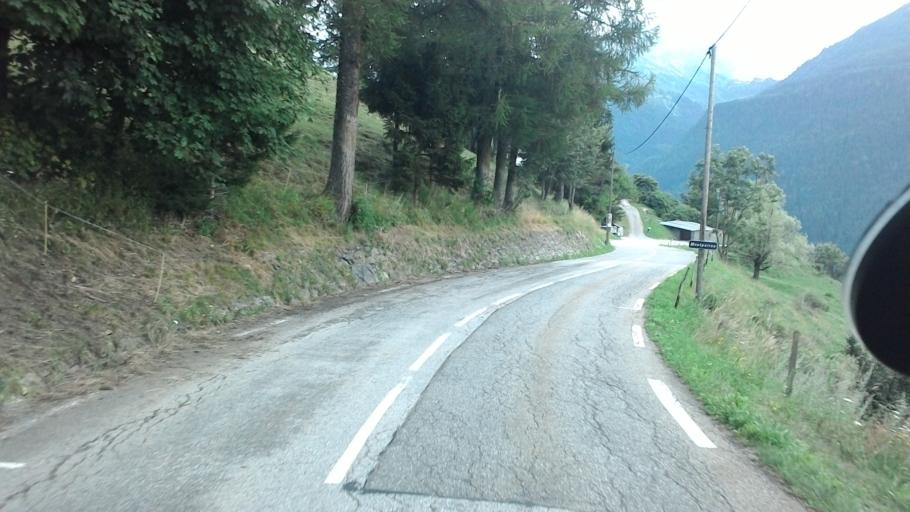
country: FR
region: Rhone-Alpes
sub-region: Departement de la Savoie
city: Seez
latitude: 45.6260
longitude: 6.8235
